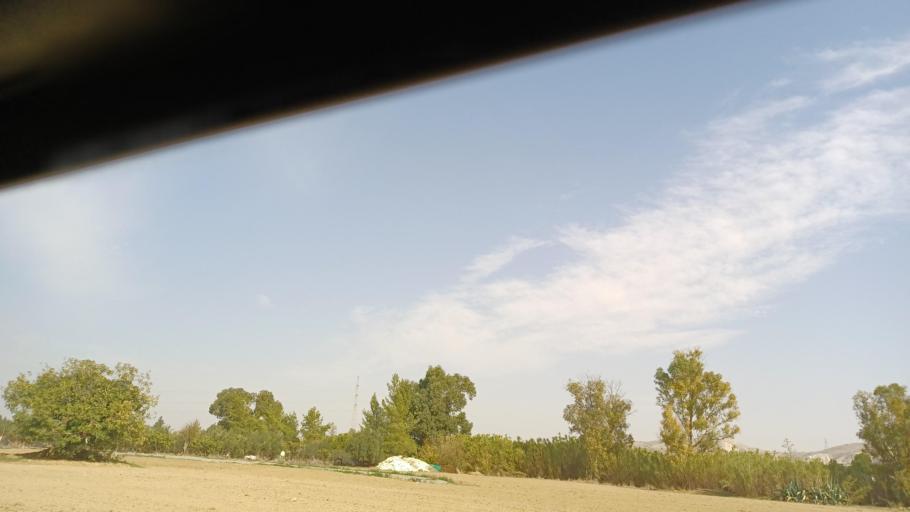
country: CY
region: Larnaka
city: Mosfiloti
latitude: 34.9688
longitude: 33.4431
